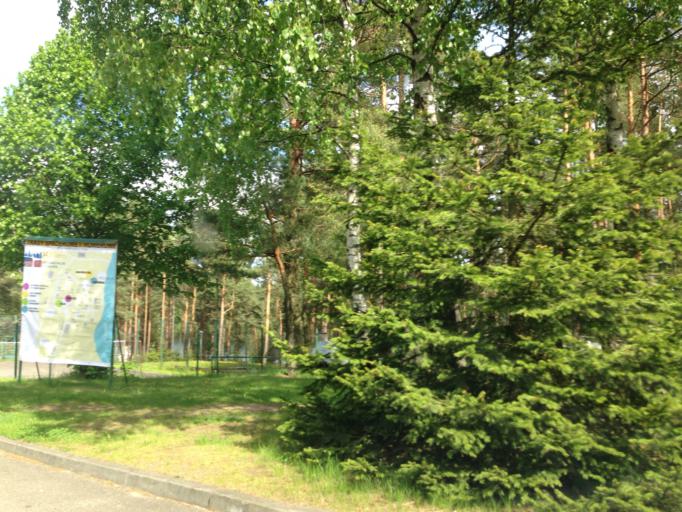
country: PL
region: Warmian-Masurian Voivodeship
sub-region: Powiat olsztynski
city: Olsztynek
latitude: 53.5037
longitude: 20.3894
